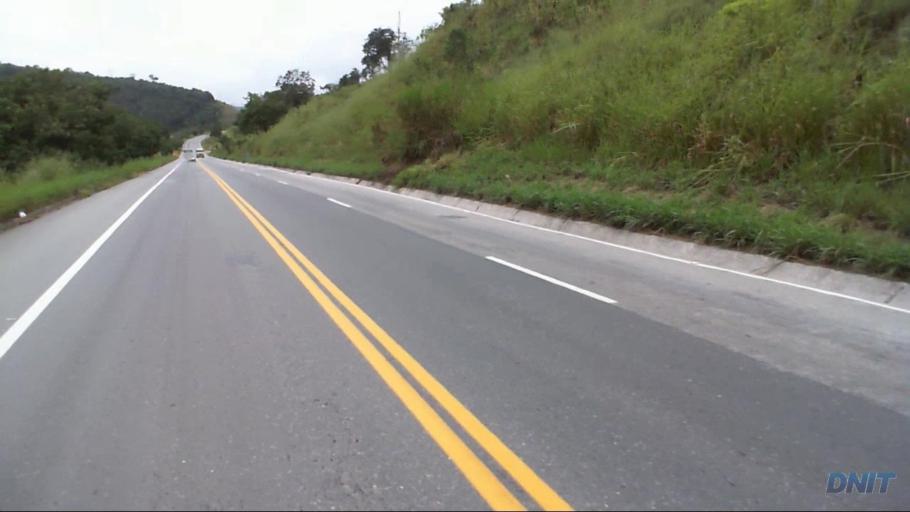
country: BR
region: Minas Gerais
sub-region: Nova Era
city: Nova Era
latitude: -19.7081
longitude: -42.9998
